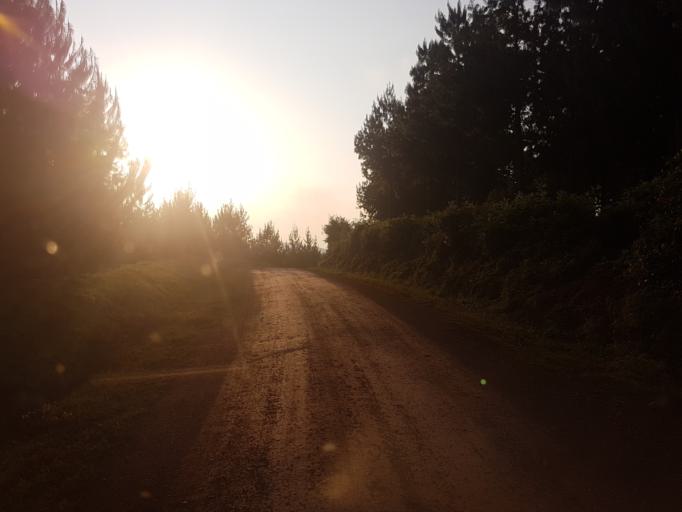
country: UG
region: Western Region
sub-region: Kanungu District
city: Kanungu
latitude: -1.0274
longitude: 29.8746
